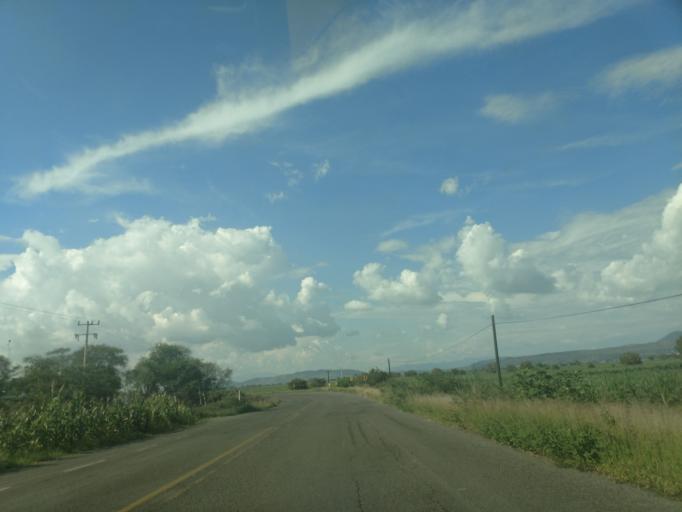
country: MX
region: Jalisco
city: Antonio Escobedo
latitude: 20.8519
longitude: -104.0284
